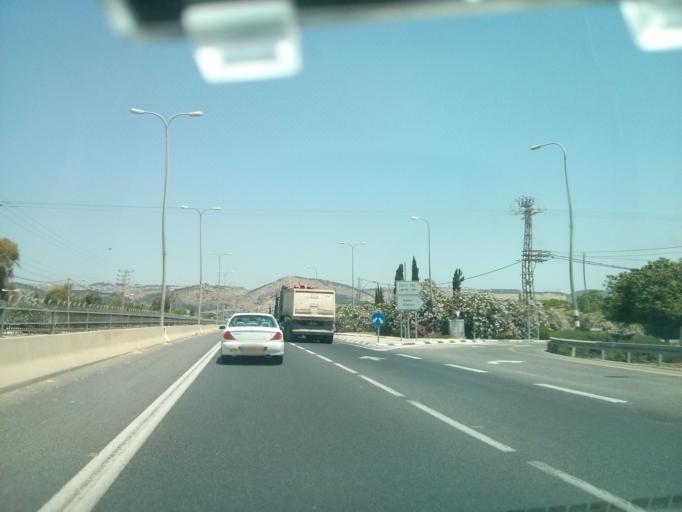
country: IL
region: Northern District
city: `Afula `Illit
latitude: 32.6394
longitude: 35.2909
